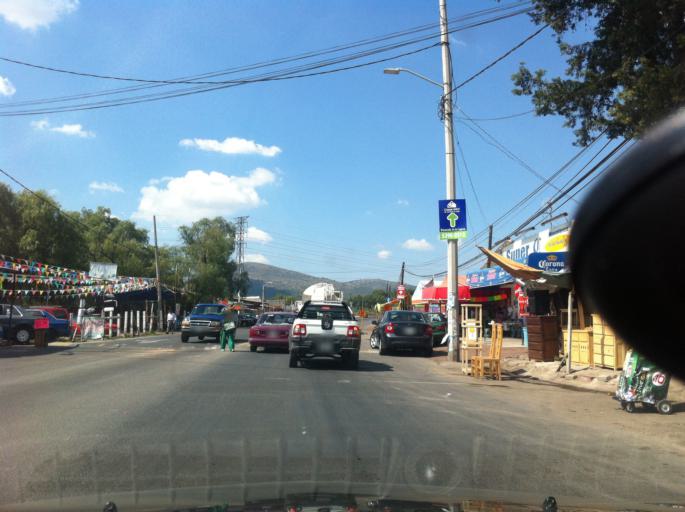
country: MX
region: Mexico
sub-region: Zumpango
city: Santa Maria de Guadalupe
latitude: 19.8145
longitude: -99.1123
